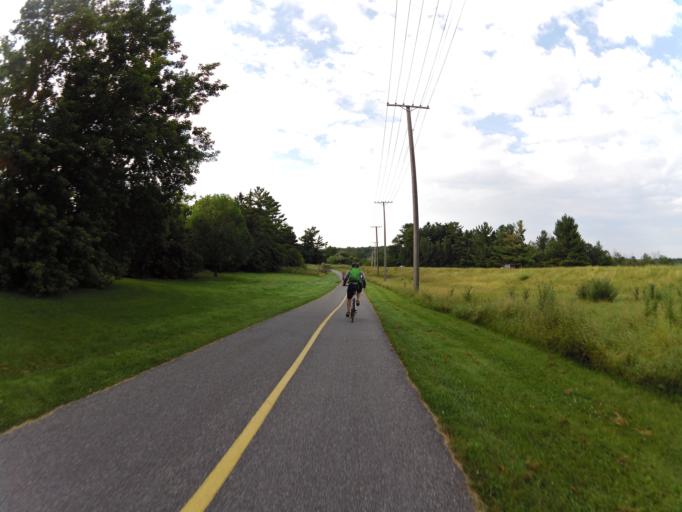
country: CA
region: Ontario
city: Ottawa
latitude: 45.4411
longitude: -75.7503
